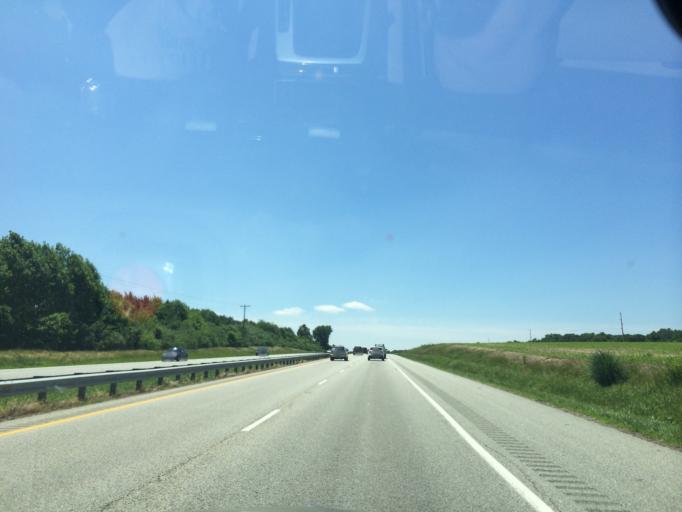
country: US
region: Maryland
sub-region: Queen Anne's County
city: Centreville
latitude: 38.9141
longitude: -76.0621
